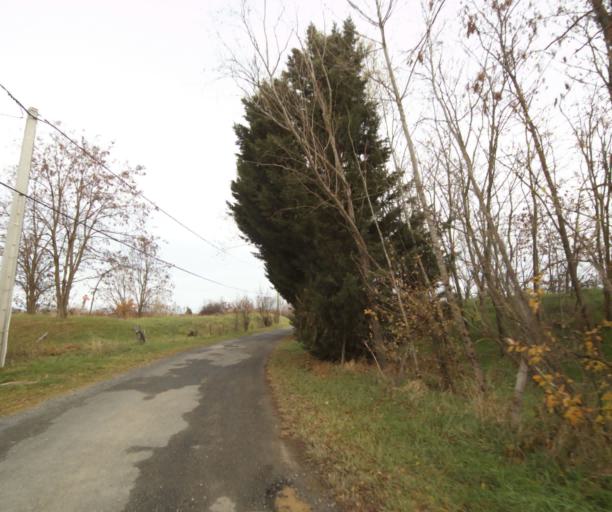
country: FR
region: Rhone-Alpes
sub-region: Departement de la Loire
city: Sury-le-Comtal
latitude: 45.5259
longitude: 4.1916
